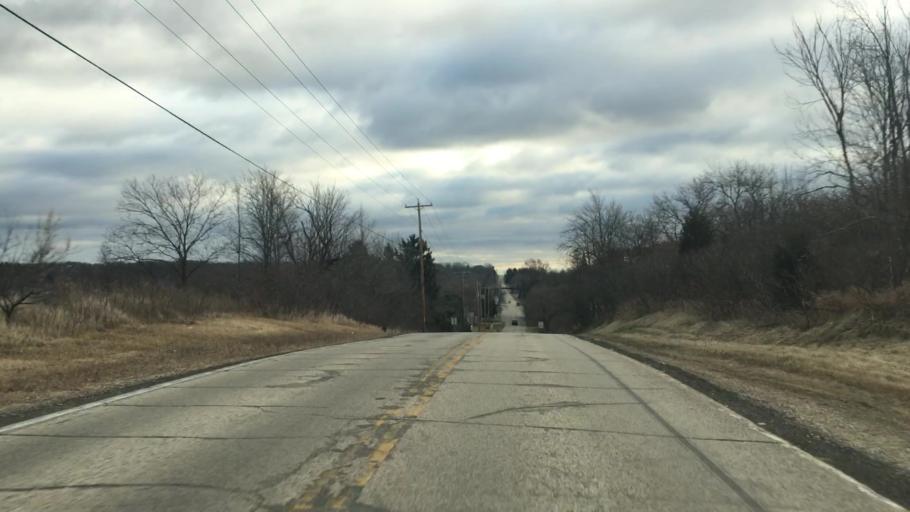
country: US
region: Wisconsin
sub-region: Washington County
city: Richfield
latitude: 43.2366
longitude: -88.2289
